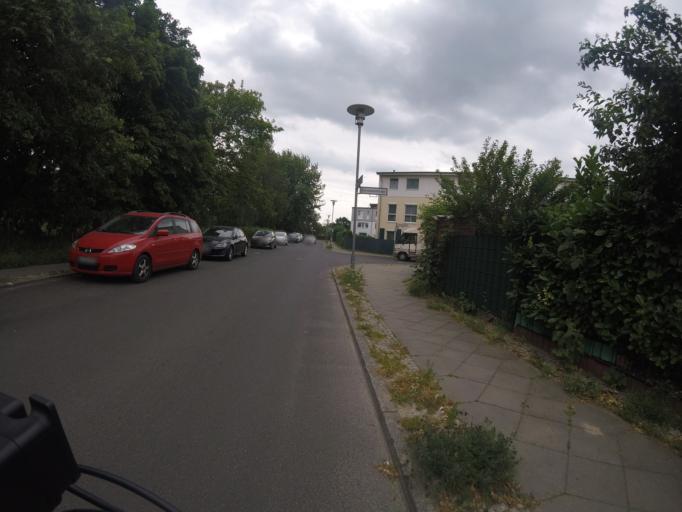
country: DE
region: Berlin
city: Haselhorst
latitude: 52.5578
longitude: 13.2312
